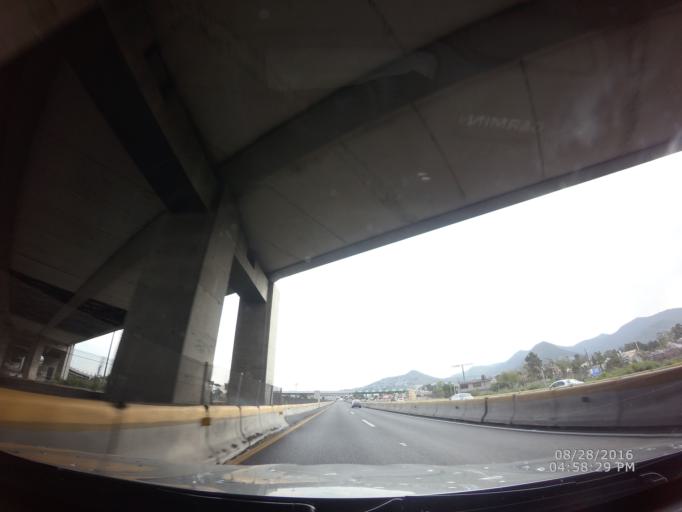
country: MX
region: Mexico
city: Ecatepec
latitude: 19.6047
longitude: -99.0371
